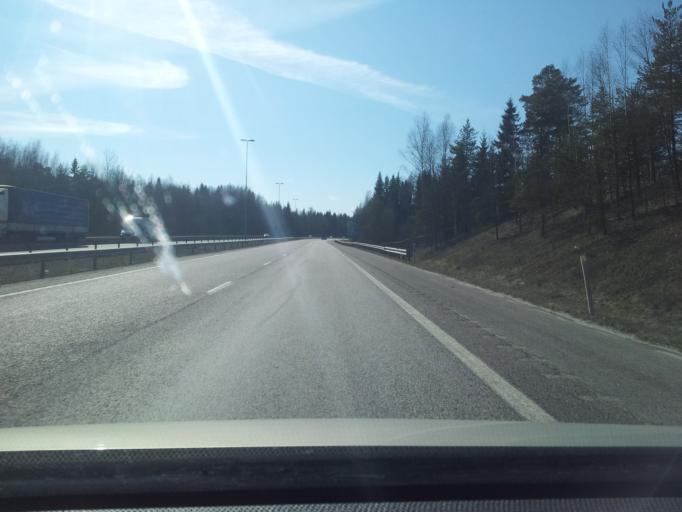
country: FI
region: Uusimaa
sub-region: Helsinki
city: Sibbo
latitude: 60.2793
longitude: 25.3121
